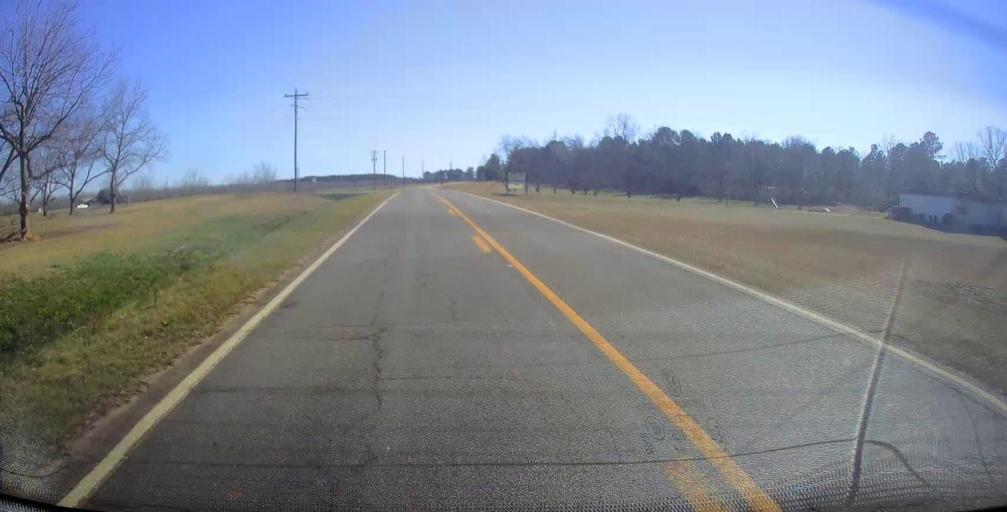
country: US
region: Georgia
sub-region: Crawford County
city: Knoxville
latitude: 32.6127
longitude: -83.9839
